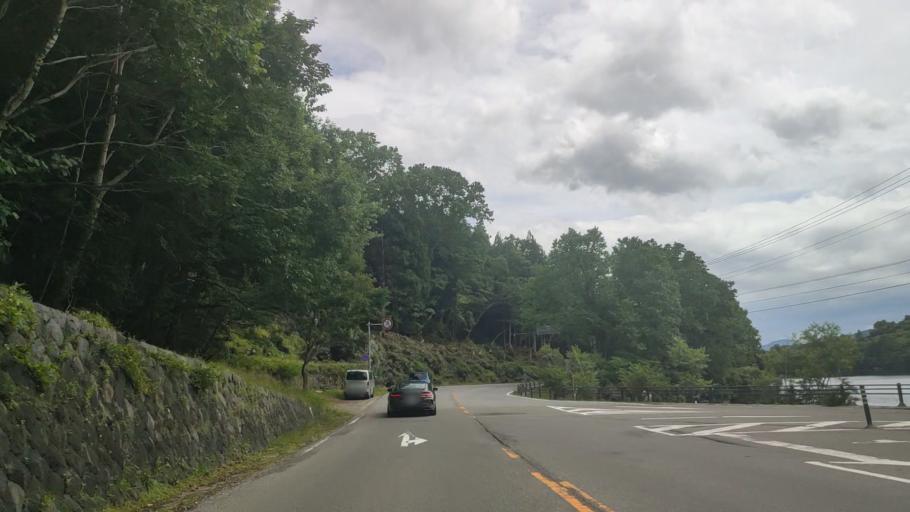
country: JP
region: Tochigi
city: Nikko
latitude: 36.8018
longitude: 139.4267
